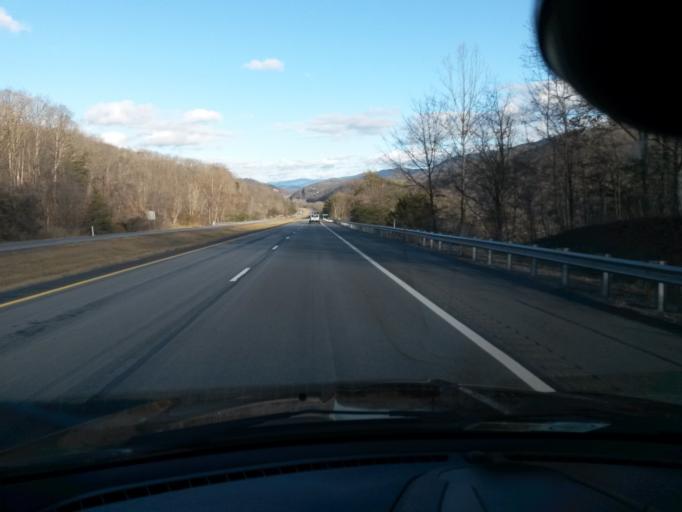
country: US
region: West Virginia
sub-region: Mercer County
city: Athens
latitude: 37.3456
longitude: -80.9307
